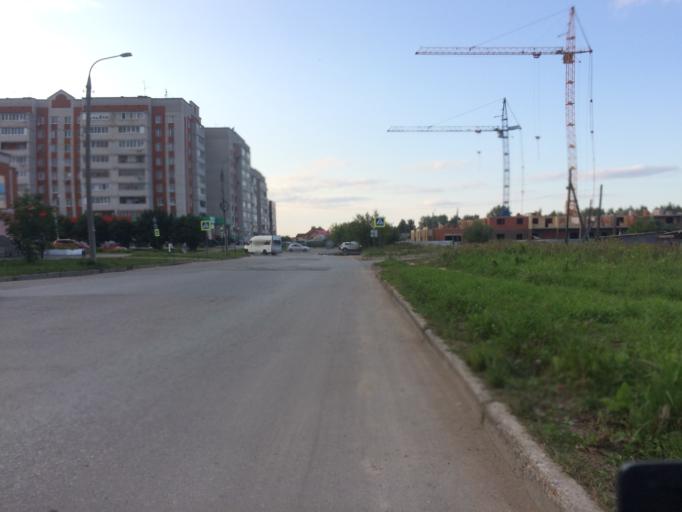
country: RU
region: Mariy-El
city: Medvedevo
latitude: 56.6441
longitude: 47.8448
